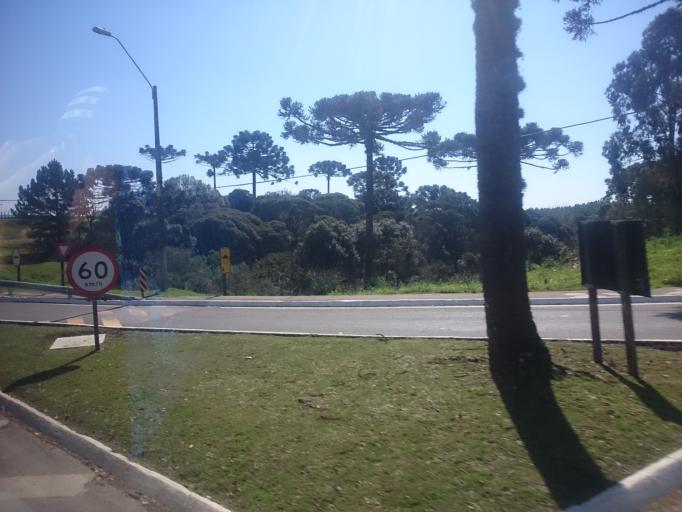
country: BR
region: Santa Catarina
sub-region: Santa Cecilia
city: Santa Cecilia
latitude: -26.9564
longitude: -50.4203
